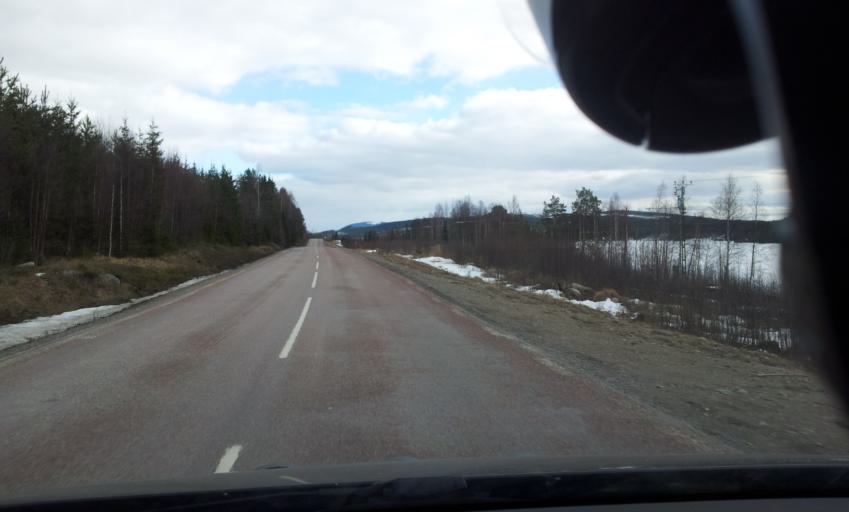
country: SE
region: Gaevleborg
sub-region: Ljusdals Kommun
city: Farila
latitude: 62.1379
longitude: 15.6899
